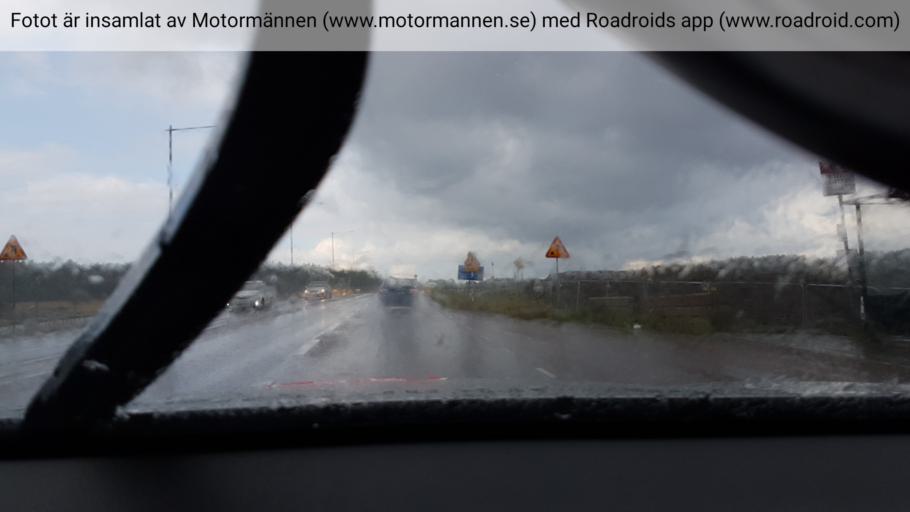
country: SE
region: Stockholm
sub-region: Ekero Kommun
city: Ekeroe
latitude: 59.3025
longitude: 17.8548
